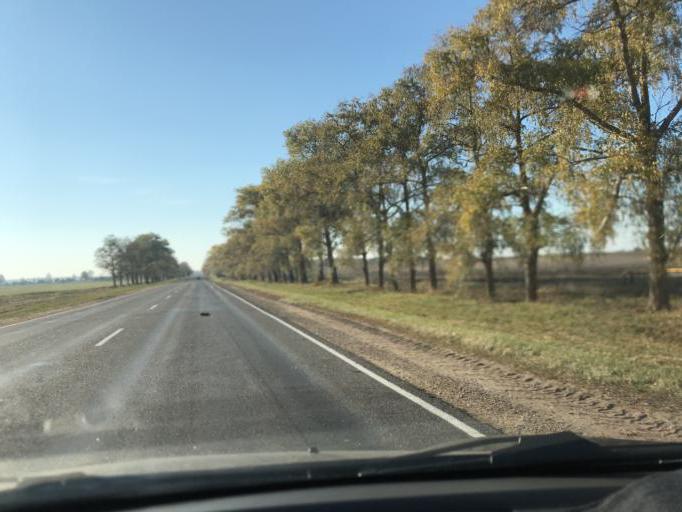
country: BY
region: Minsk
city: Staryya Darohi
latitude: 53.0561
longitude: 28.4346
